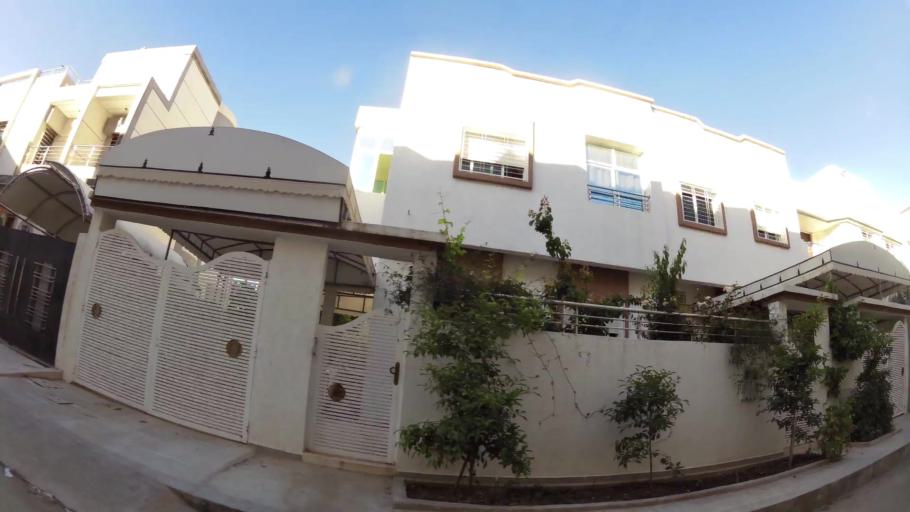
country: MA
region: Fes-Boulemane
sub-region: Fes
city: Fes
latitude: 34.0083
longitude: -5.0106
